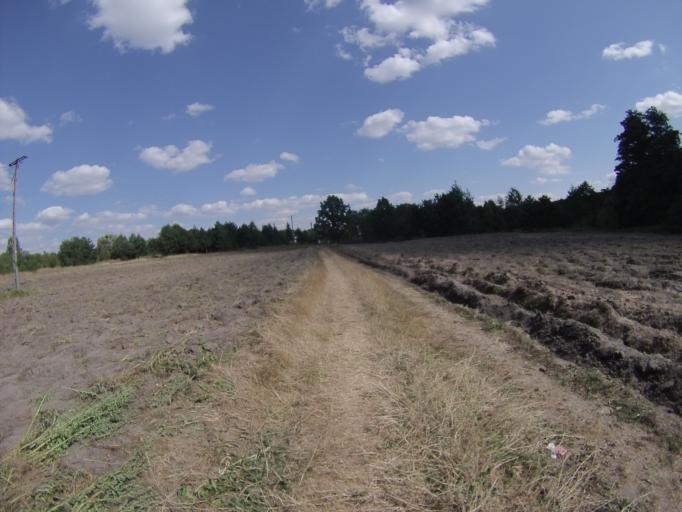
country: PL
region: Swietokrzyskie
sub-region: Powiat kielecki
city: Rakow
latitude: 50.7023
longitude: 21.0537
